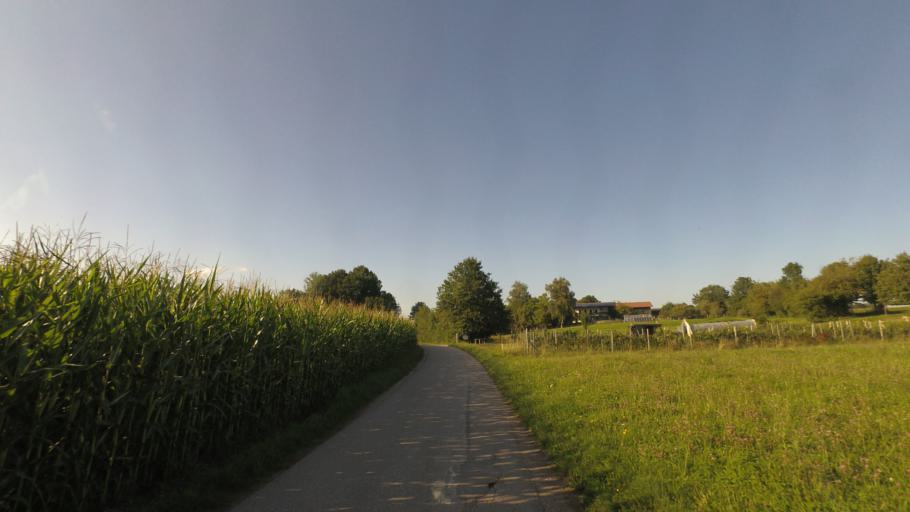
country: DE
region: Bavaria
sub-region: Upper Bavaria
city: Chieming
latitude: 47.8848
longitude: 12.5384
